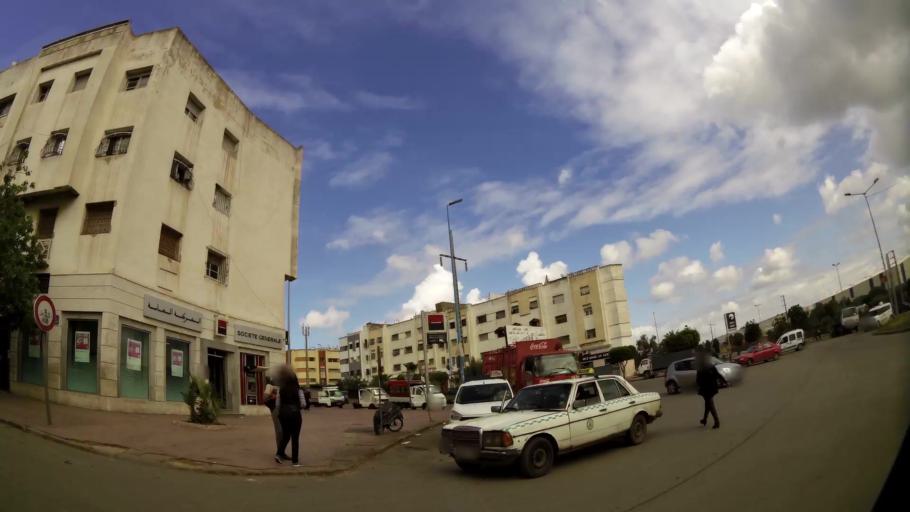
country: MA
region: Grand Casablanca
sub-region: Mediouna
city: Tit Mellil
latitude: 33.5981
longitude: -7.4857
